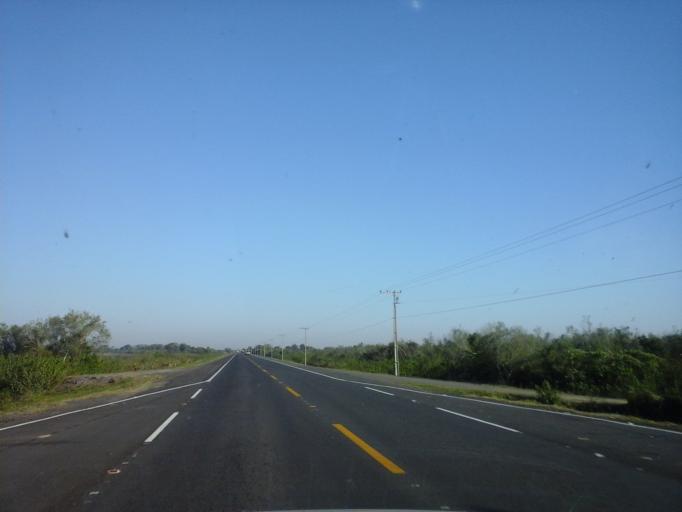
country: PY
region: Neembucu
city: Pilar
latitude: -26.8563
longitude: -58.1932
